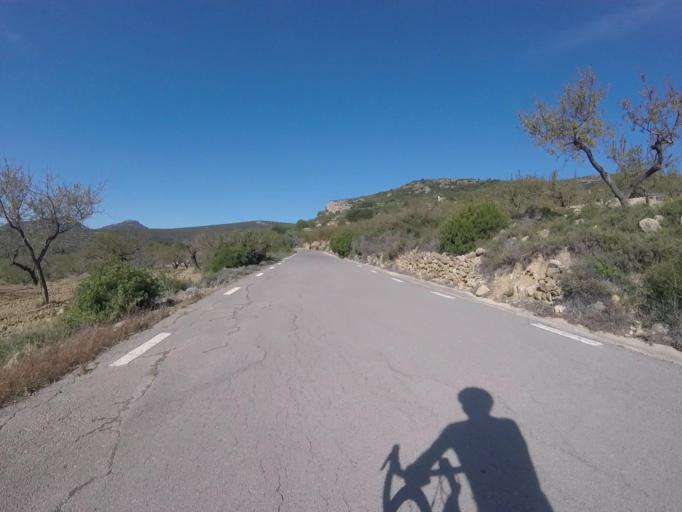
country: ES
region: Valencia
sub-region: Provincia de Castello
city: Sarratella
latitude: 40.2769
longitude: 0.0360
